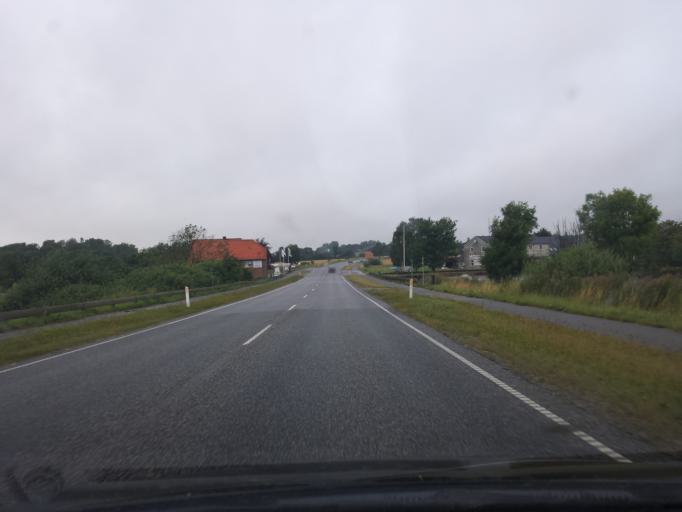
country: DK
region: South Denmark
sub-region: Sonderborg Kommune
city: Guderup
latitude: 54.9756
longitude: 9.8882
